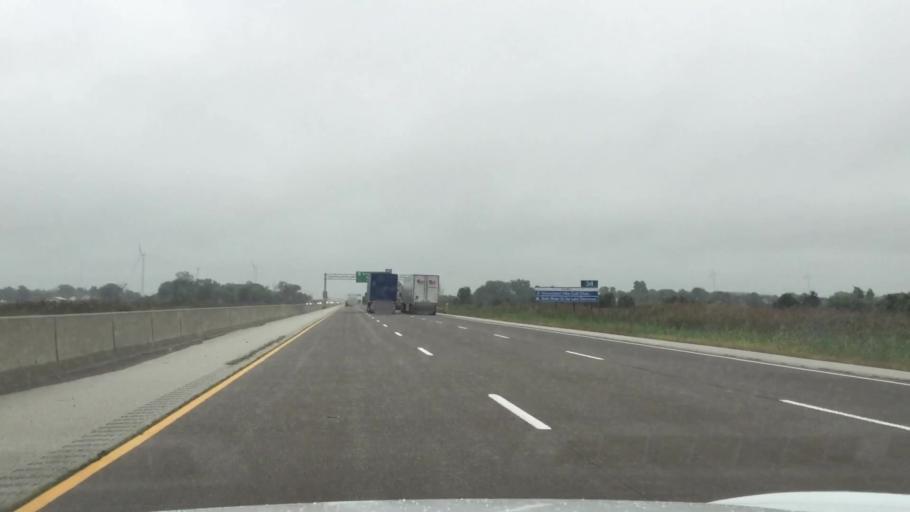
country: US
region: Michigan
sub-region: Wayne County
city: Grosse Pointe
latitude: 42.2371
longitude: -82.7274
